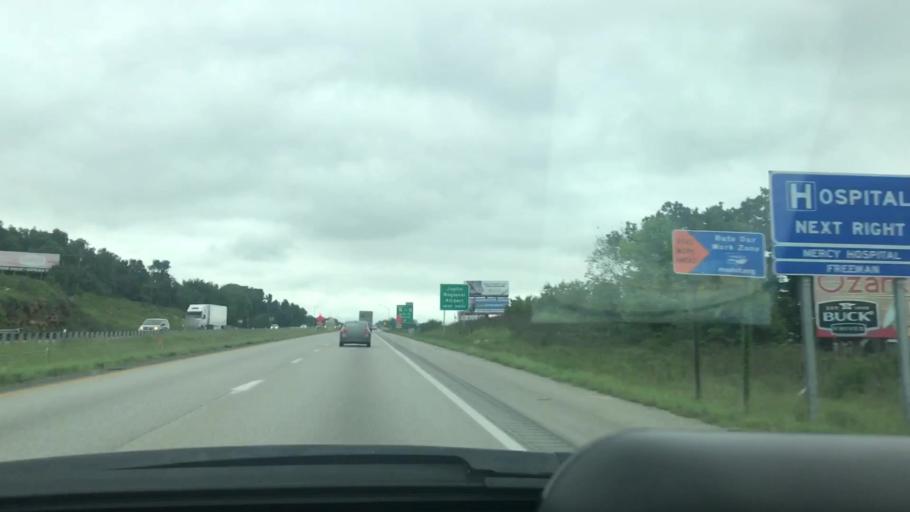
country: US
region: Missouri
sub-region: Jasper County
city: Joplin
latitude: 37.0315
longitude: -94.5220
